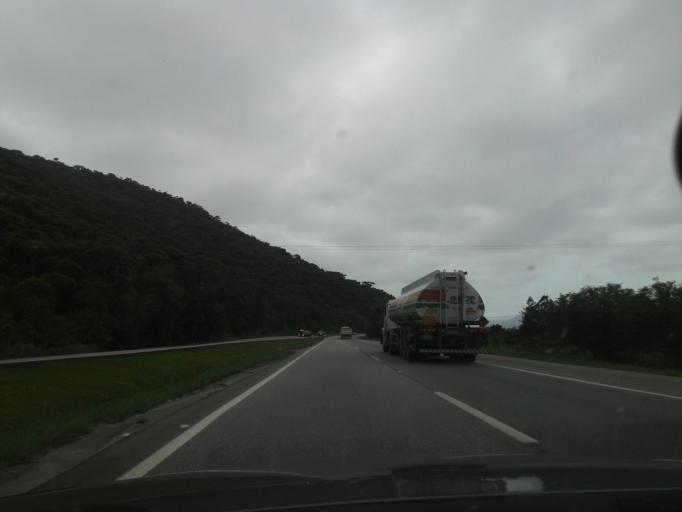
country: BR
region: Santa Catarina
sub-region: Florianopolis
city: Pantano do Sul
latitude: -27.8550
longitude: -48.6425
